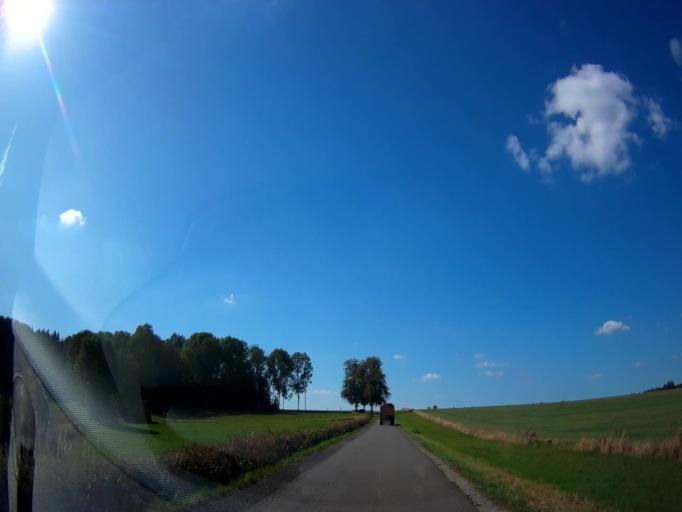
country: BE
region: Wallonia
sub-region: Province de Namur
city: Houyet
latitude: 50.2352
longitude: 4.9709
